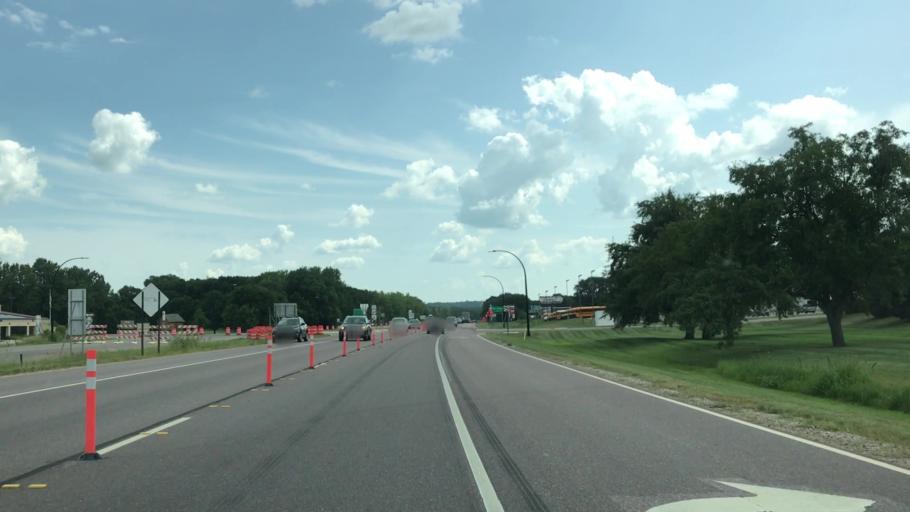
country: US
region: Minnesota
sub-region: Nicollet County
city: Saint Peter
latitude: 44.3500
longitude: -93.9521
